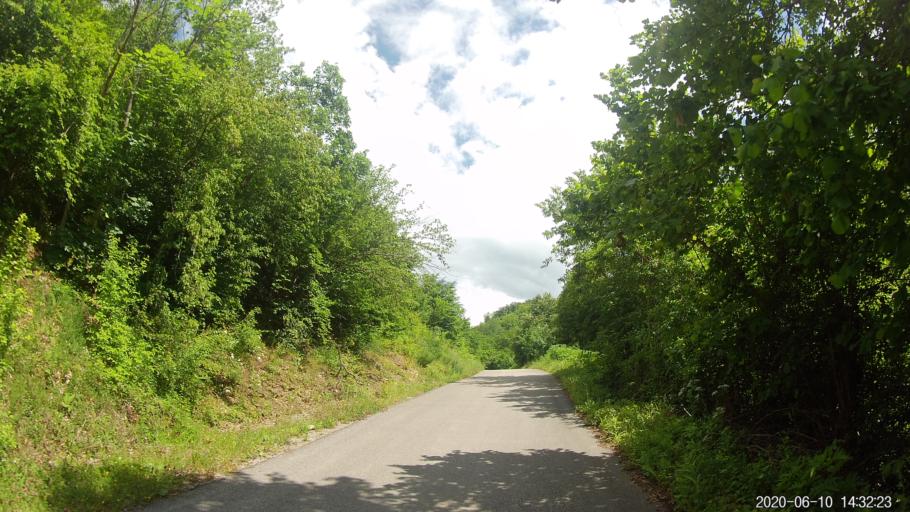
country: XK
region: Prizren
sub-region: Komuna e Therandes
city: Budakovo
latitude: 42.4164
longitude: 20.9246
